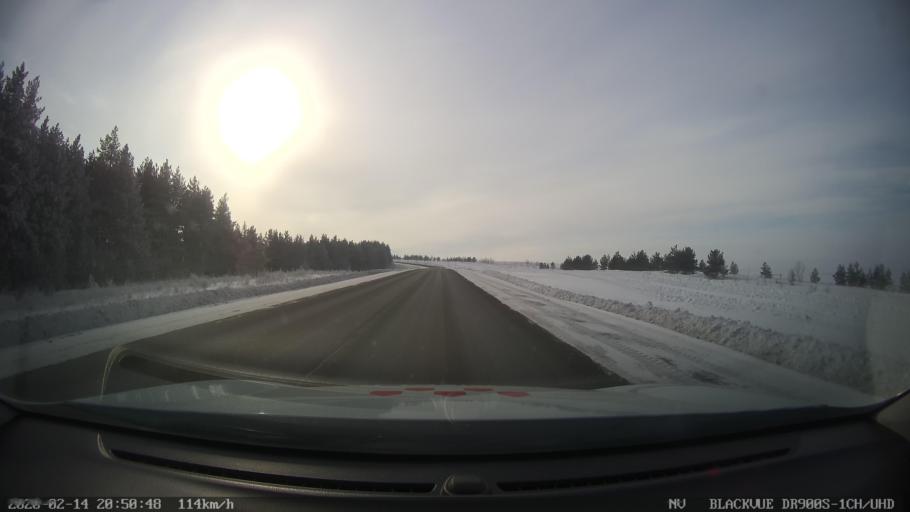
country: RU
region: Tatarstan
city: Kuybyshevskiy Zaton
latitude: 55.2217
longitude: 49.2321
